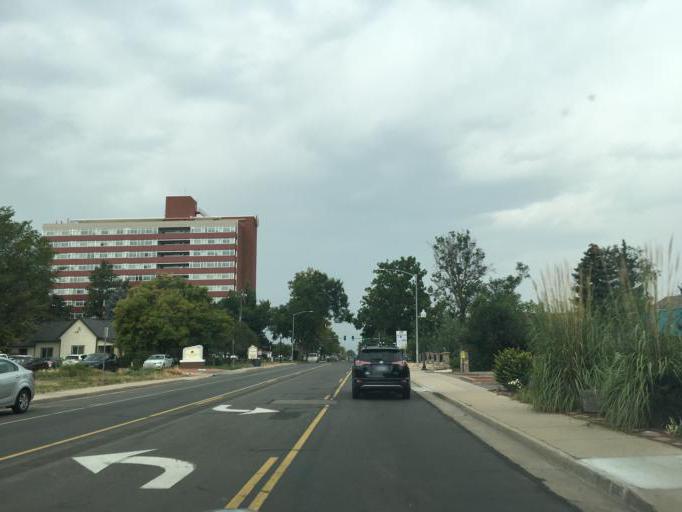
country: US
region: Colorado
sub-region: Jefferson County
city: Wheat Ridge
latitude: 39.7694
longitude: -105.0650
